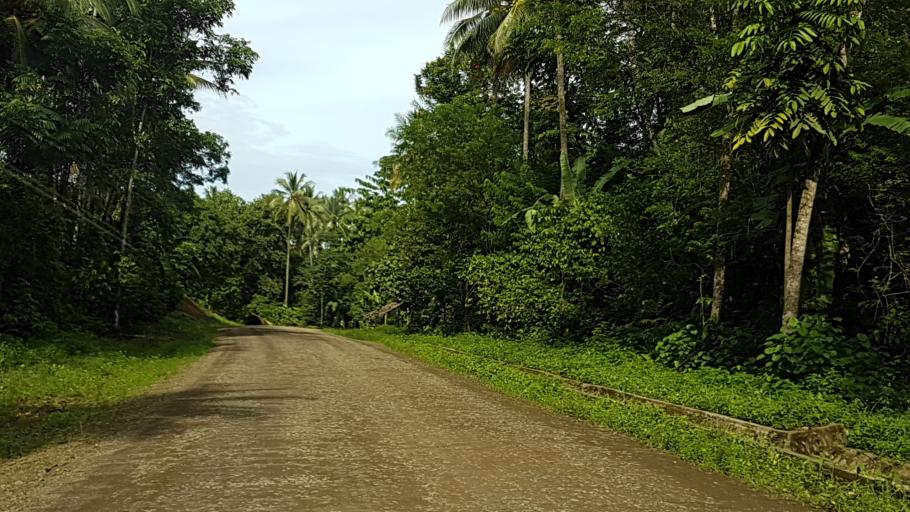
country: PG
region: Milne Bay
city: Alotau
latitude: -10.3228
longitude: 150.6669
